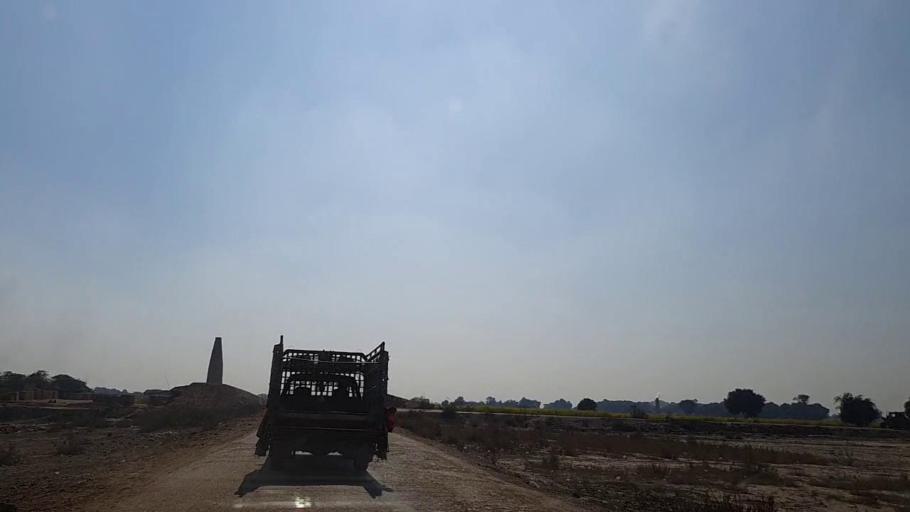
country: PK
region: Sindh
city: Sakrand
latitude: 26.2916
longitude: 68.1080
